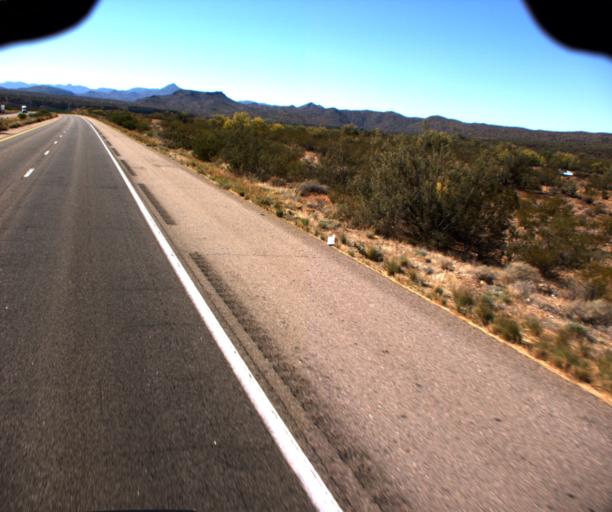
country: US
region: Arizona
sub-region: Yavapai County
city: Bagdad
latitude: 34.6513
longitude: -113.5726
